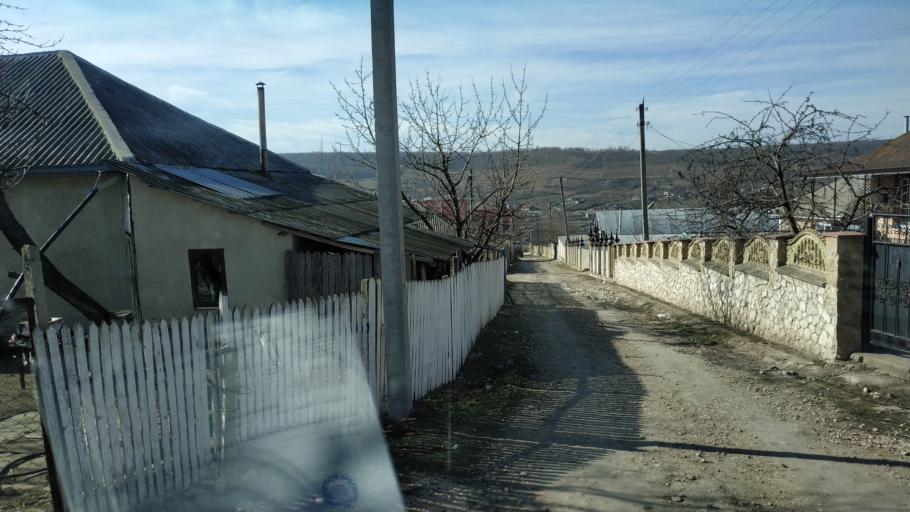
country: MD
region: Chisinau
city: Vatra
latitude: 47.0312
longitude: 28.6320
